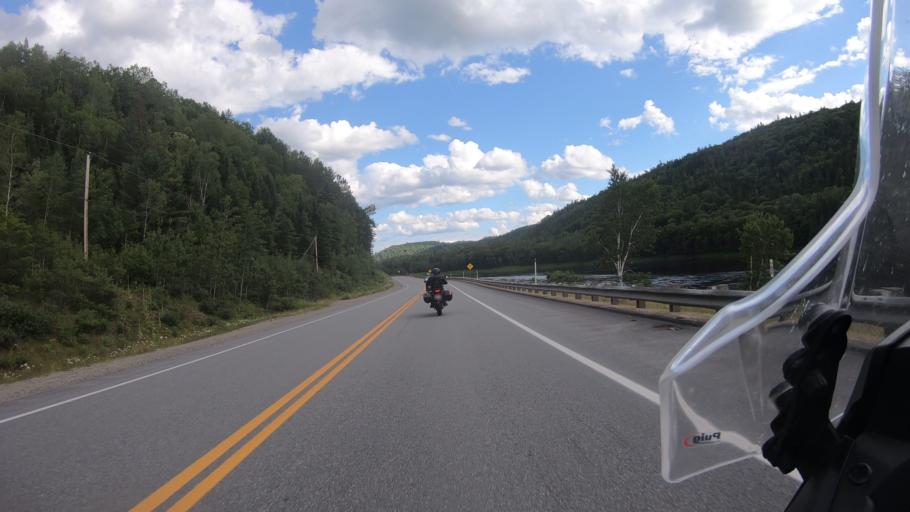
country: CA
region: Quebec
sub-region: Mauricie
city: Saint-Tite
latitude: 47.0009
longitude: -72.9244
